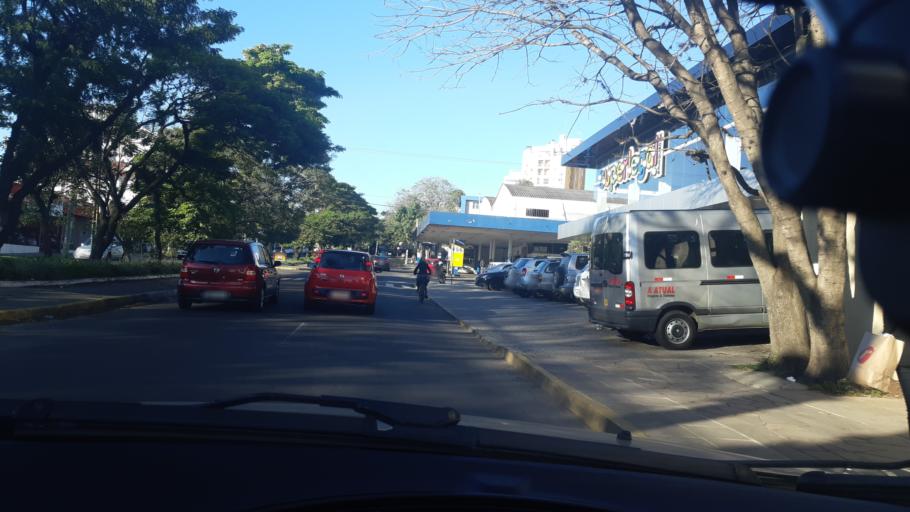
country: BR
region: Rio Grande do Sul
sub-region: Sao Leopoldo
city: Sao Leopoldo
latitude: -29.7698
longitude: -51.1395
